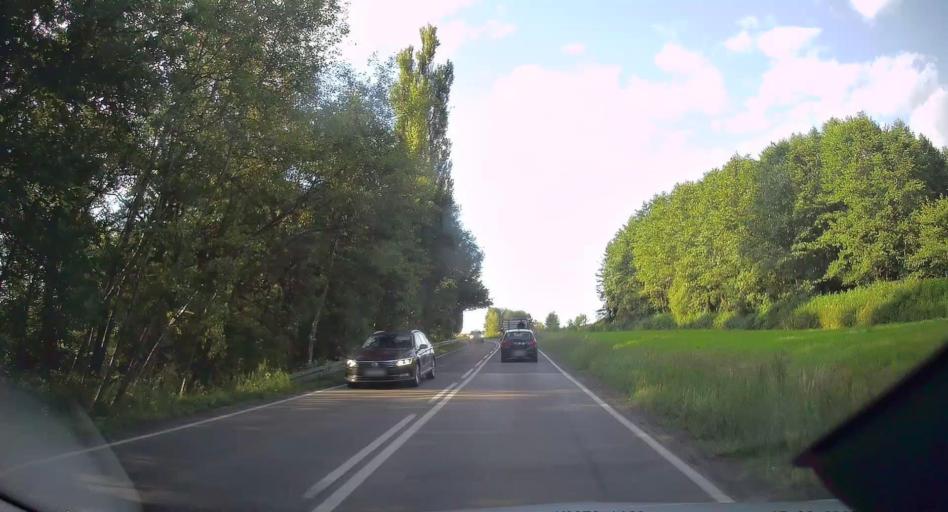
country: PL
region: Lesser Poland Voivodeship
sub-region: Powiat oswiecimski
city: Grojec
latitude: 49.9755
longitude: 19.2219
